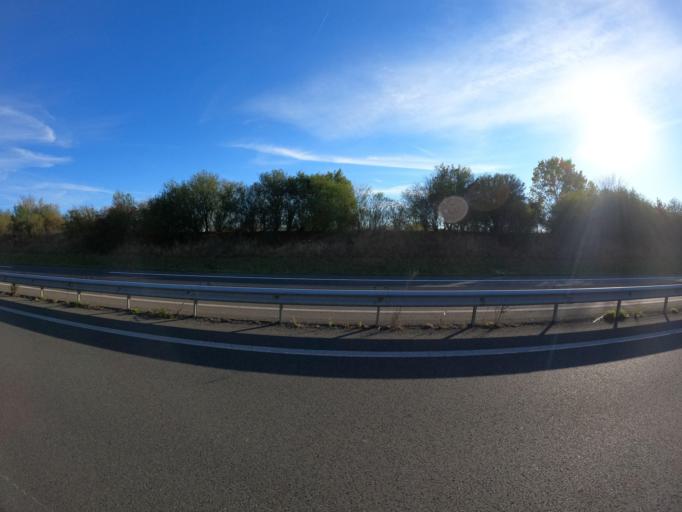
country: FR
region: Pays de la Loire
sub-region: Departement de Maine-et-Loire
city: Saint-Lambert-du-Lattay
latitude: 47.2422
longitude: -0.6571
